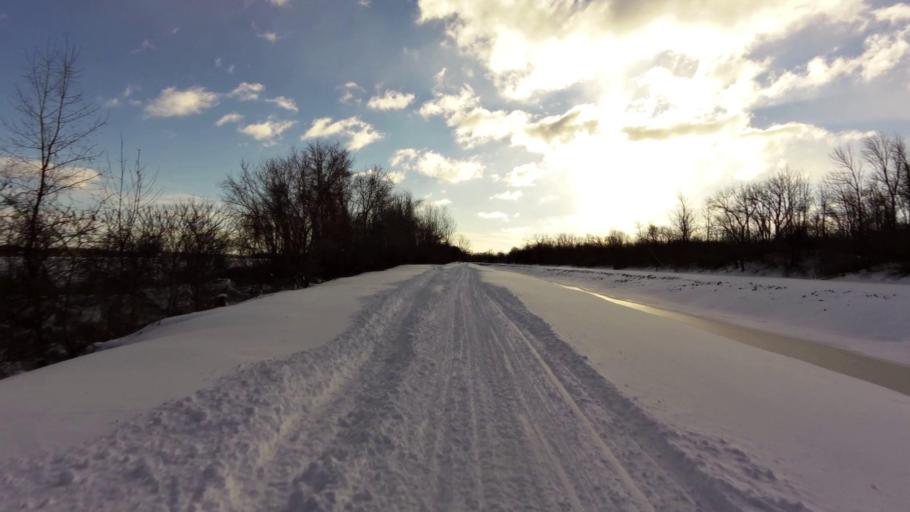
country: US
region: New York
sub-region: Orleans County
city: Albion
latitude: 43.2494
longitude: -78.1436
